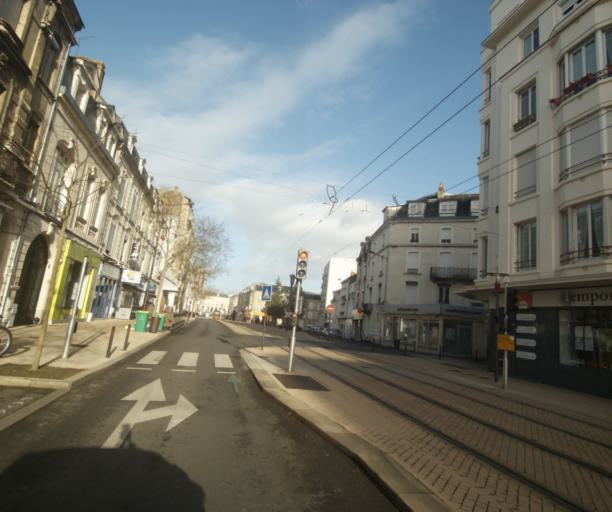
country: FR
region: Pays de la Loire
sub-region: Departement de la Sarthe
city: Le Mans
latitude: 47.9996
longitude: 0.1961
